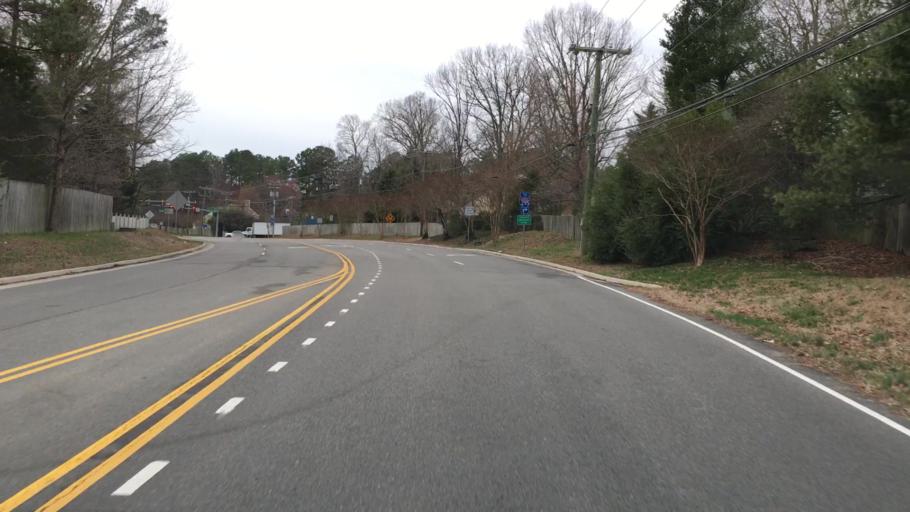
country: US
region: Virginia
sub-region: Henrico County
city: Short Pump
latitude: 37.6646
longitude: -77.5619
